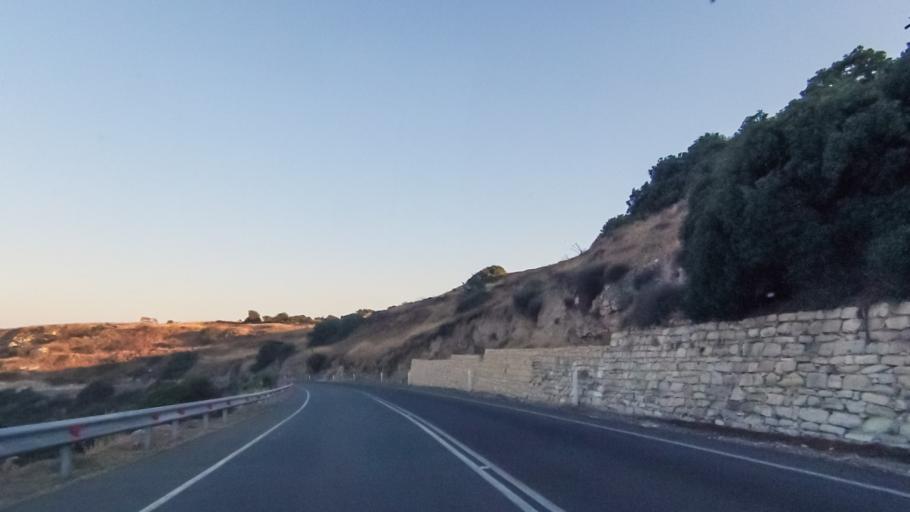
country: CY
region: Limassol
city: Erimi
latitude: 34.6678
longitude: 32.8853
